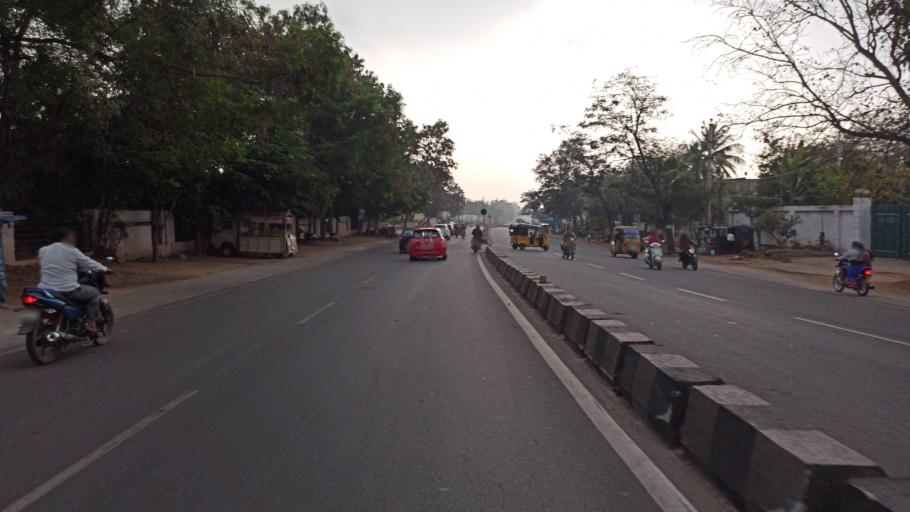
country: IN
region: Telangana
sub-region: Rangareddi
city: Uppal Kalan
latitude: 17.4013
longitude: 78.5456
